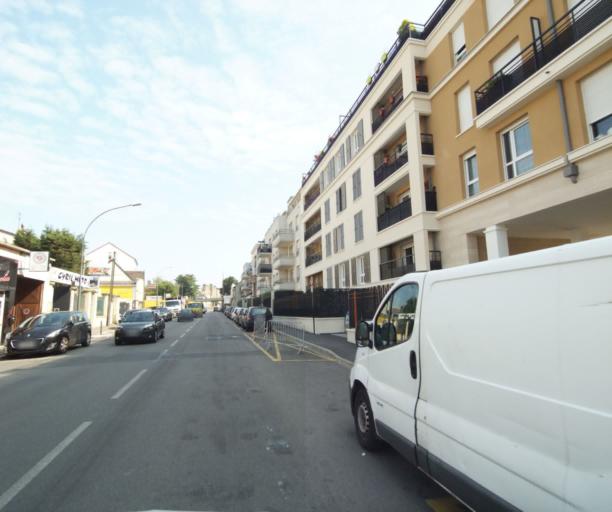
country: FR
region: Ile-de-France
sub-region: Departement du Val-d'Oise
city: Argenteuil
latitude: 48.9508
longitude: 2.2537
